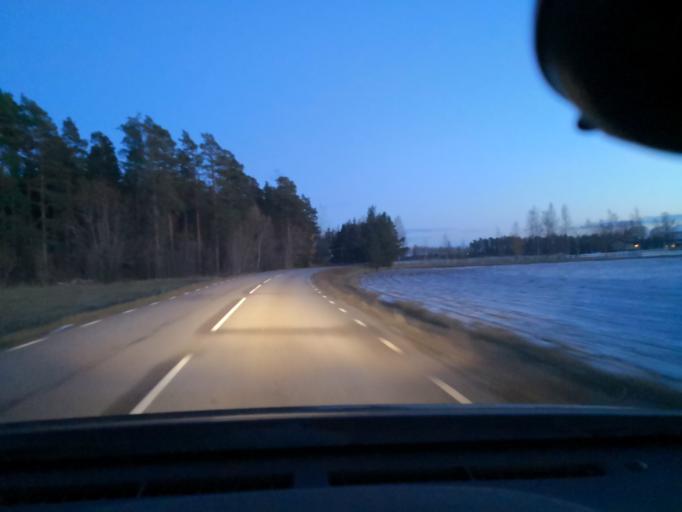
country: SE
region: Vaestmanland
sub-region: Sala Kommun
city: Sala
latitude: 59.8742
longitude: 16.7020
